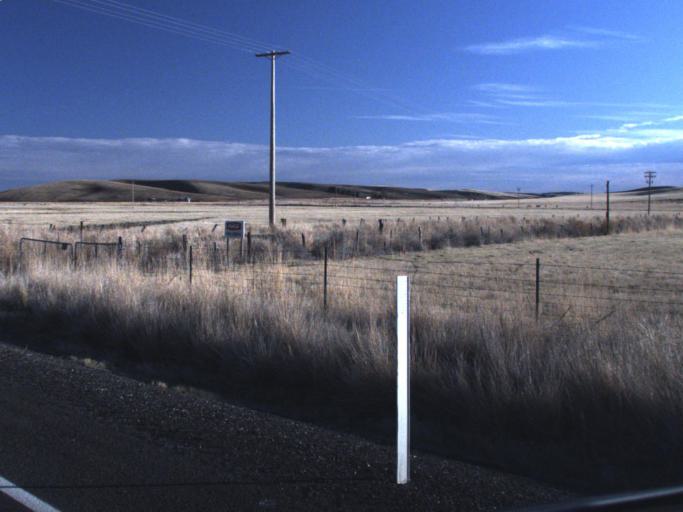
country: US
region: Washington
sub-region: Garfield County
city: Pomeroy
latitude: 46.7665
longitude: -117.7110
